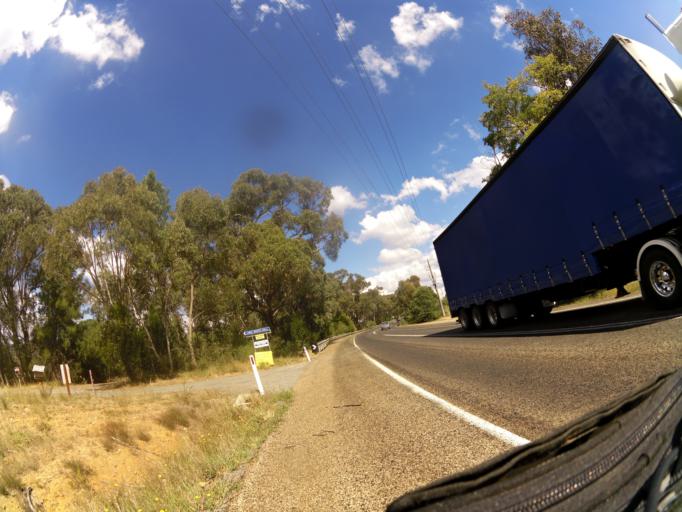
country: AU
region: Victoria
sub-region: Mansfield
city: Mansfield
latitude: -36.8292
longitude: 146.0086
